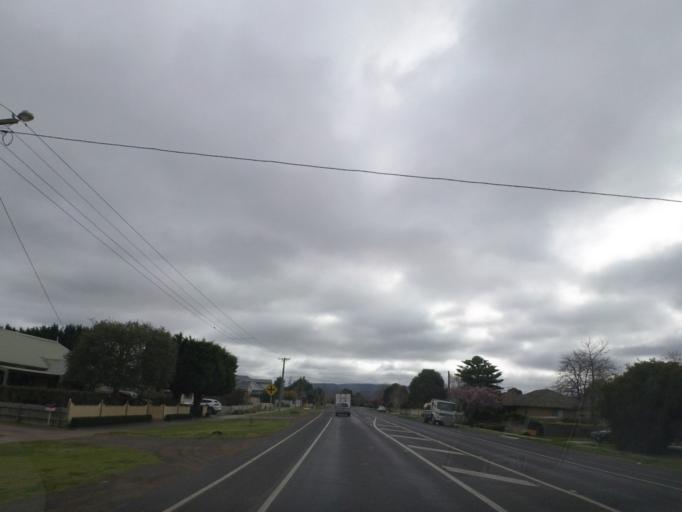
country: AU
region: Victoria
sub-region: Whittlesea
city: Whittlesea
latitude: -37.5126
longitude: 145.1154
